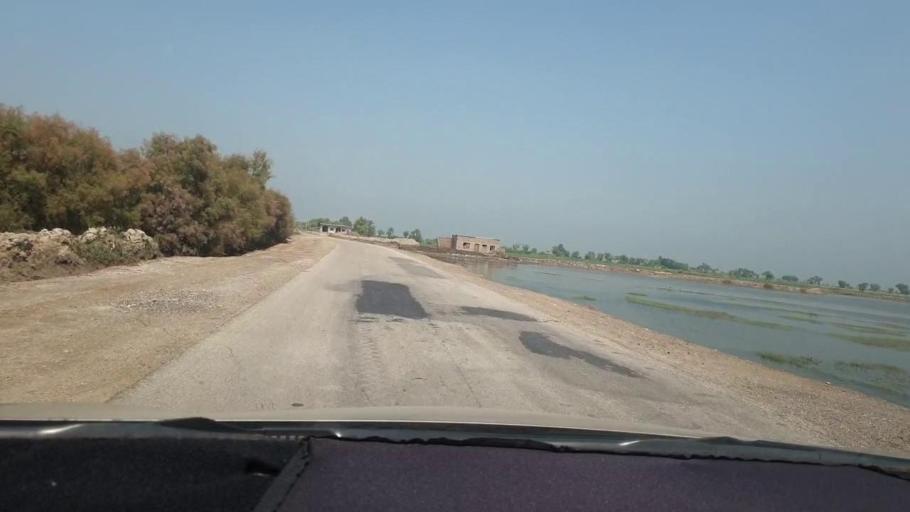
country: PK
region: Sindh
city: Miro Khan
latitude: 27.8158
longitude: 68.0273
